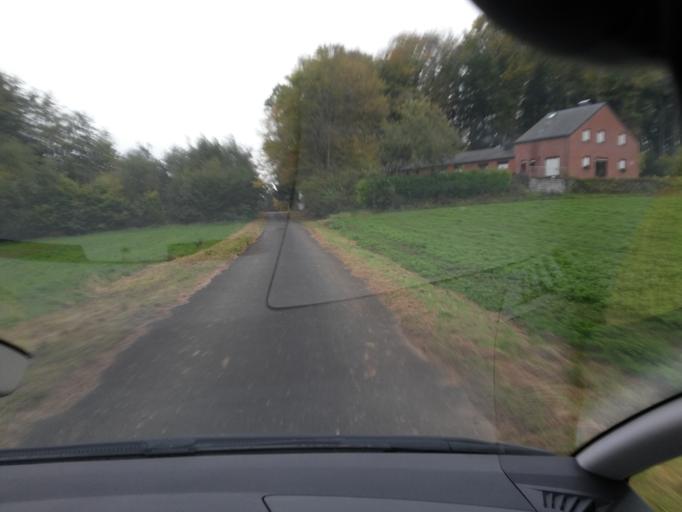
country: BE
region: Wallonia
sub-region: Province du Luxembourg
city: Arlon
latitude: 49.7127
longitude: 5.8113
